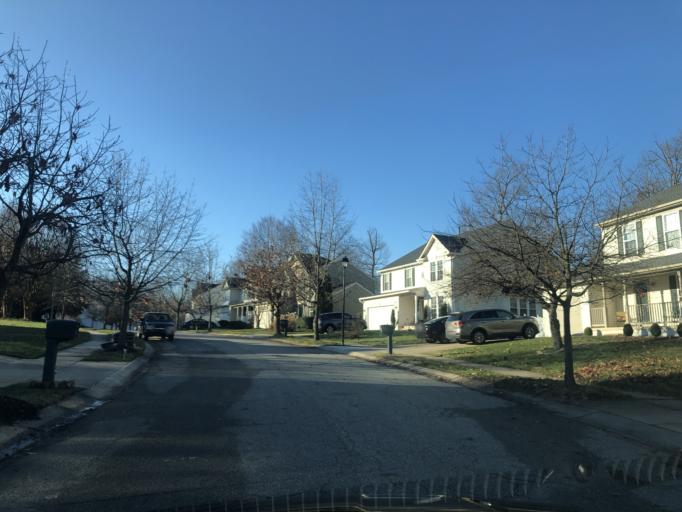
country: US
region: Maryland
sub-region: Anne Arundel County
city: Odenton
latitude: 39.0826
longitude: -76.7039
